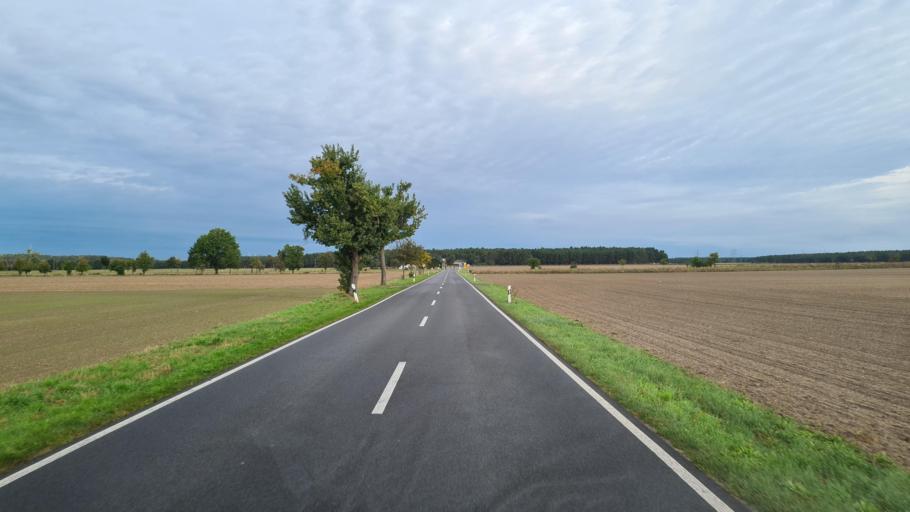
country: DE
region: Brandenburg
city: Luckau
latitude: 51.8800
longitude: 13.7202
